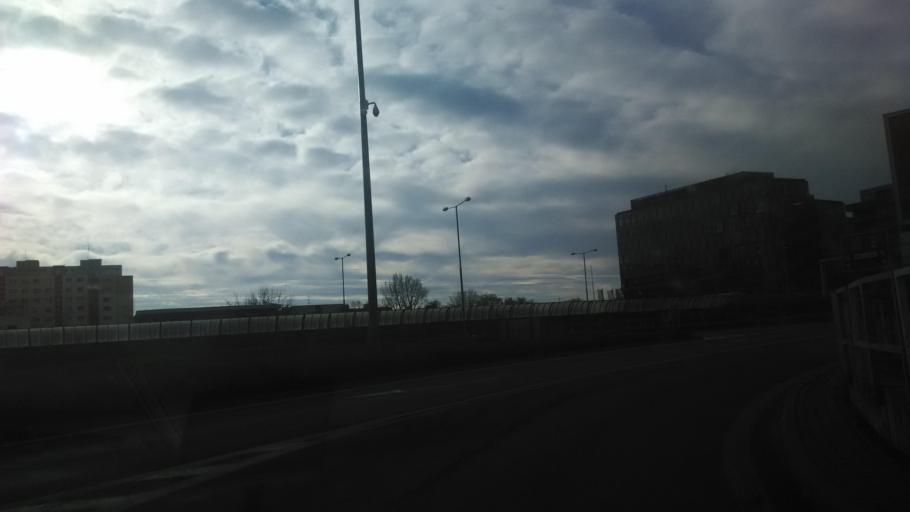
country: SK
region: Bratislavsky
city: Bratislava
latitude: 48.1324
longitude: 17.1109
